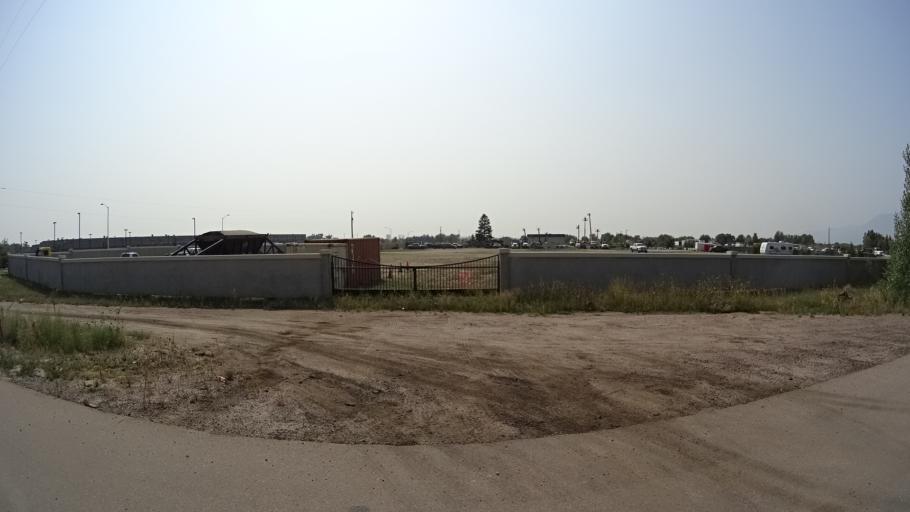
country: US
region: Colorado
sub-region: El Paso County
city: Cimarron Hills
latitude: 38.8356
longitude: -104.7256
